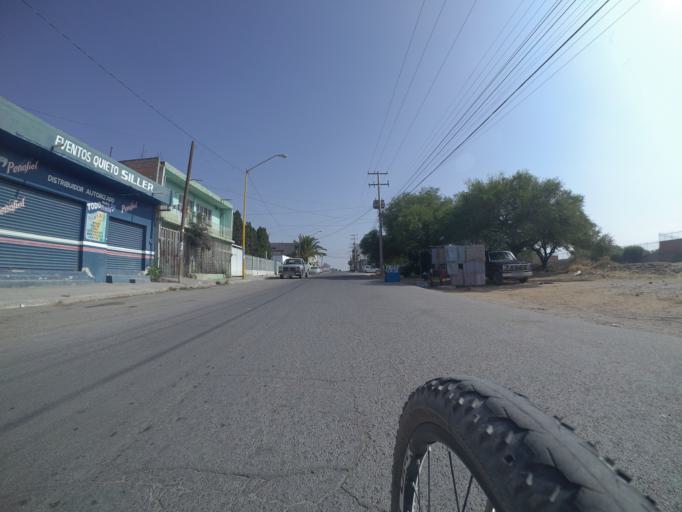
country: MX
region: Aguascalientes
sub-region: Jesus Maria
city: Jesus Maria
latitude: 21.9656
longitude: -102.3423
